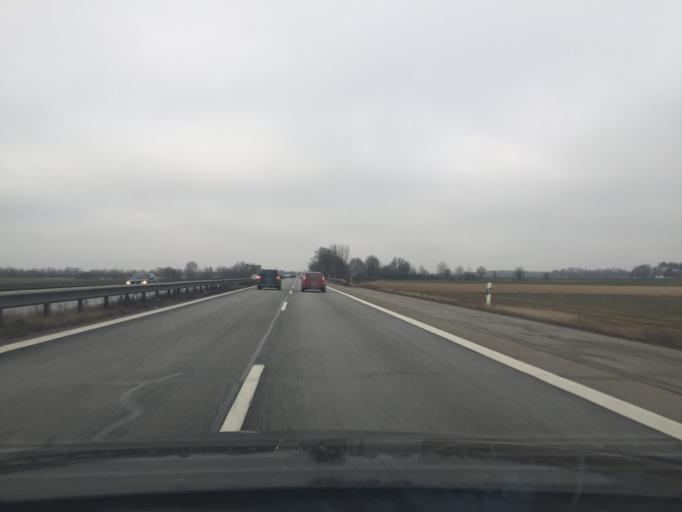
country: DE
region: Bavaria
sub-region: Upper Bavaria
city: Ottobrunn
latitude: 48.0462
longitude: 11.6481
